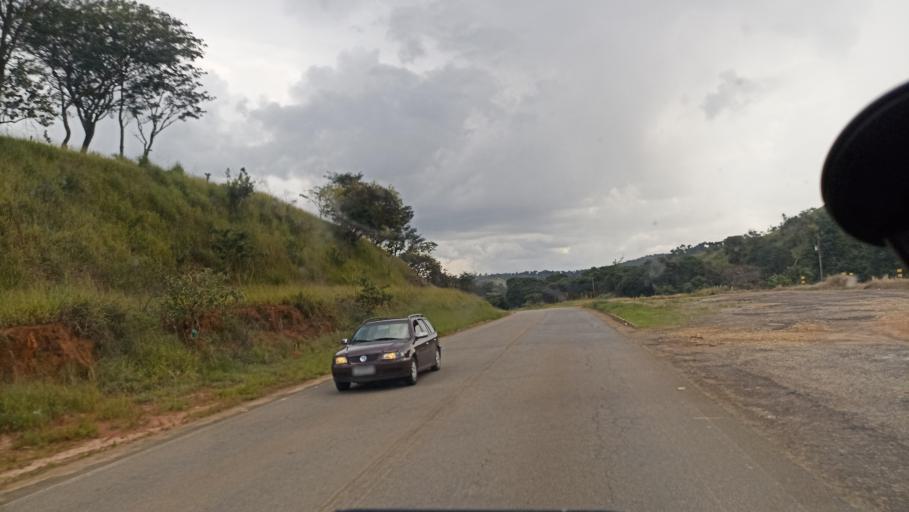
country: BR
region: Minas Gerais
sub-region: Cruzilia
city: Cruzilia
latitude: -21.8915
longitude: -44.8162
